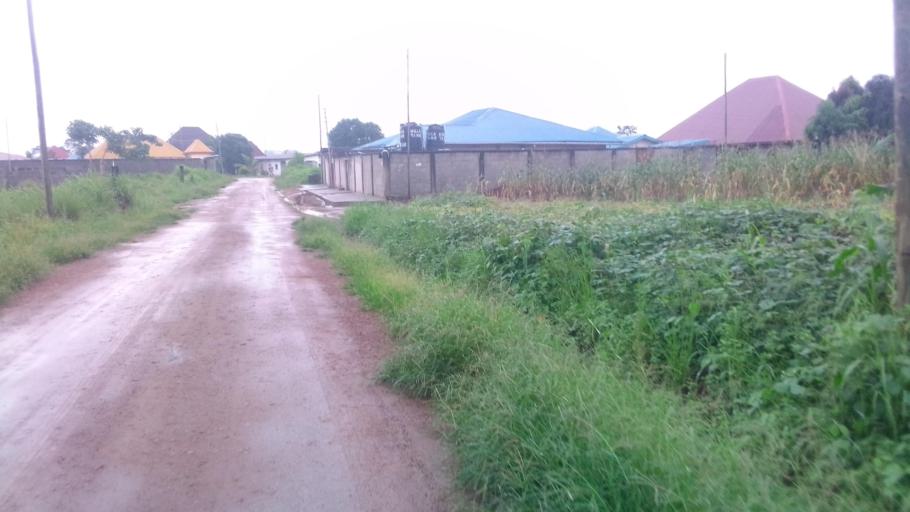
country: SL
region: Eastern Province
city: Hangha
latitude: 7.9109
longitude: -11.1637
